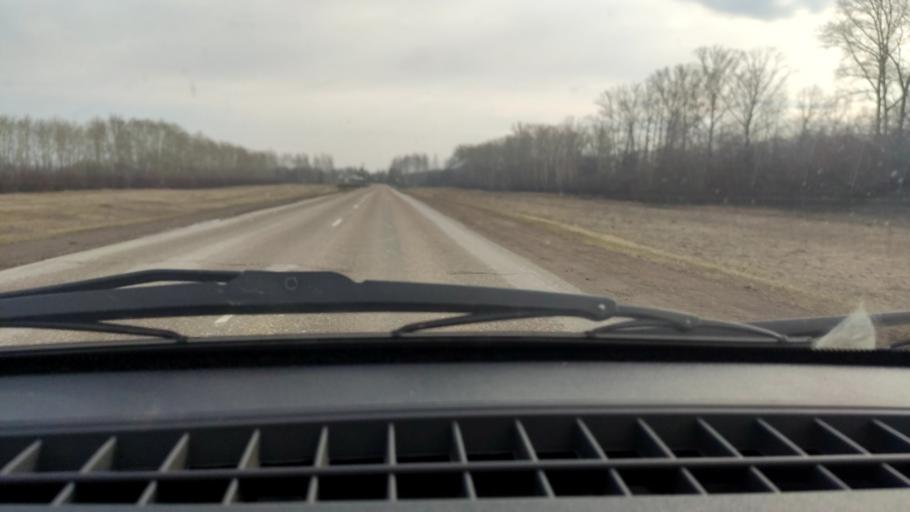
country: RU
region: Bashkortostan
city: Davlekanovo
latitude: 54.3584
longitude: 55.1905
